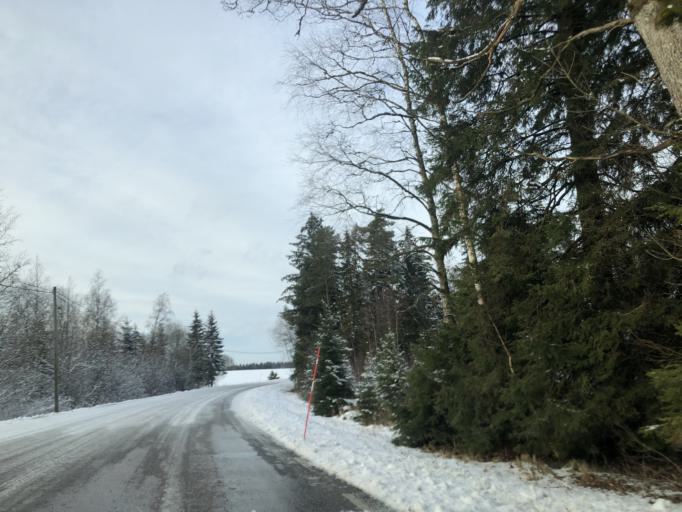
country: SE
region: Vaestra Goetaland
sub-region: Ulricehamns Kommun
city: Ulricehamn
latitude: 57.8108
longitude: 13.5383
